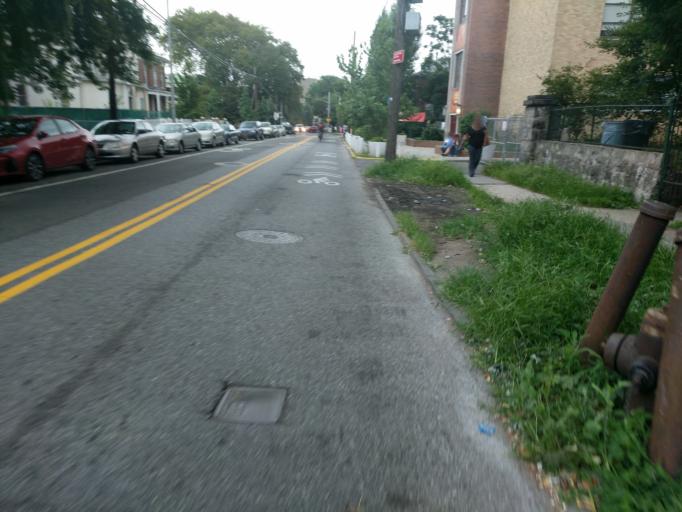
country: US
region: New York
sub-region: Queens County
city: Long Island City
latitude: 40.7738
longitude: -73.9308
